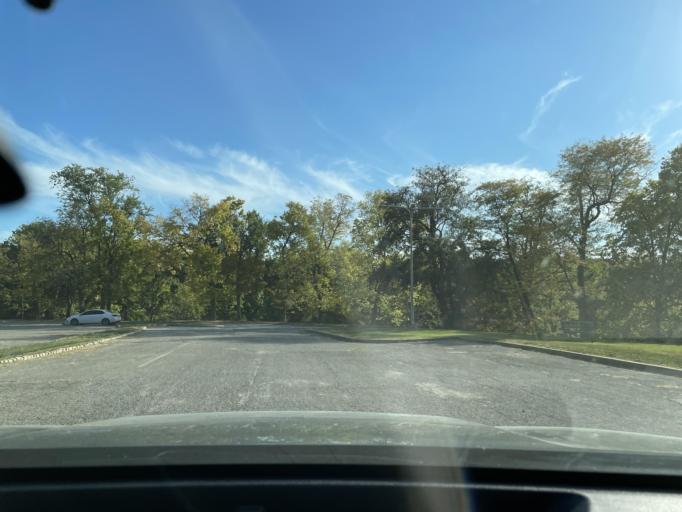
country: US
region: Missouri
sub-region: Buchanan County
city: Saint Joseph
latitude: 39.8001
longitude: -94.8529
